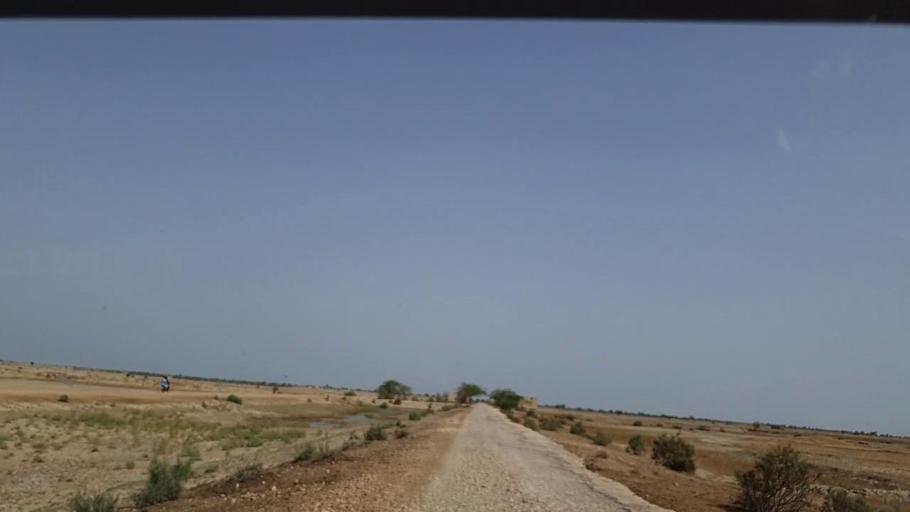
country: PK
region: Sindh
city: Johi
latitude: 26.7668
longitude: 67.6596
